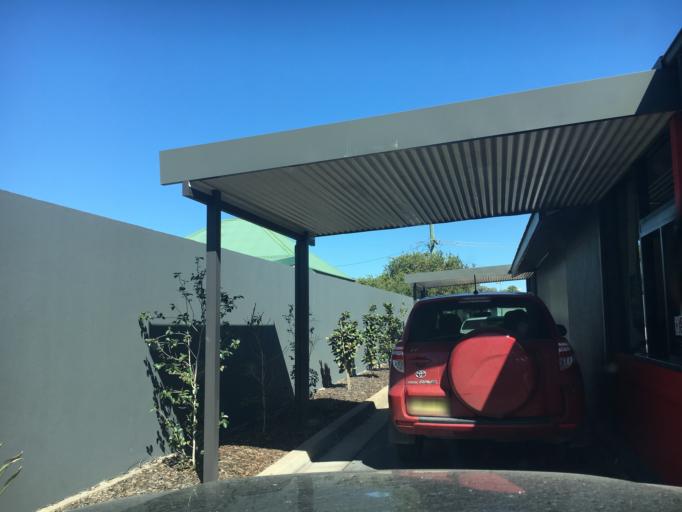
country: AU
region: New South Wales
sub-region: Singleton
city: Singleton
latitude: -32.5684
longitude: 151.1805
